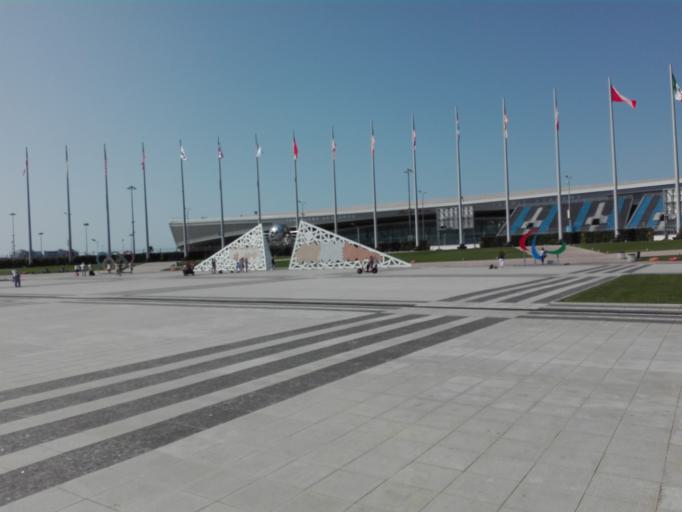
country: RU
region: Krasnodarskiy
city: Adler
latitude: 43.4068
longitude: 39.9548
